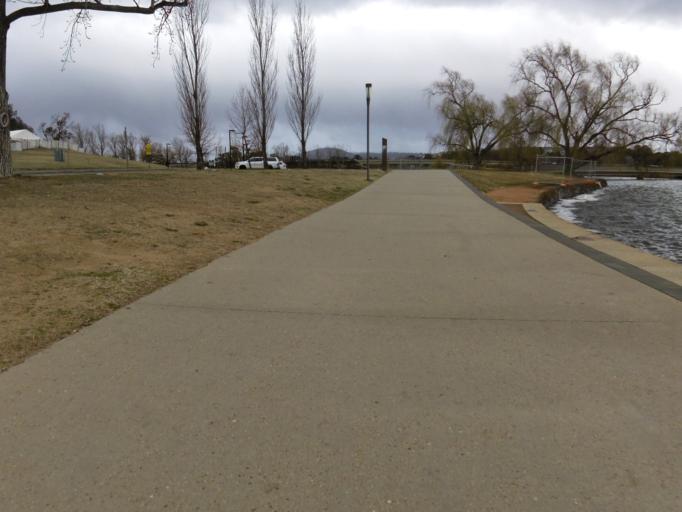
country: AU
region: Australian Capital Territory
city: Canberra
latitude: -35.2979
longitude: 149.1434
